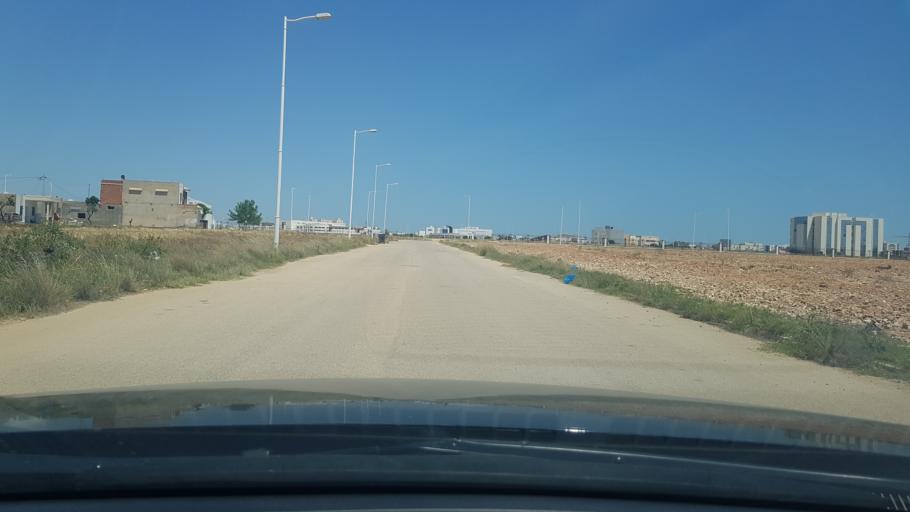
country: TN
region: Safaqis
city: Al Qarmadah
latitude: 34.8341
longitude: 10.7474
